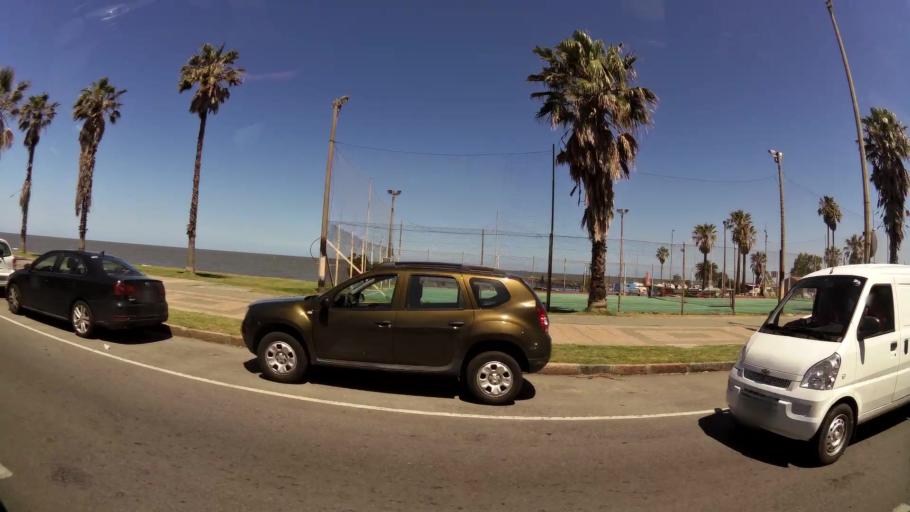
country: UY
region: Montevideo
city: Montevideo
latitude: -34.9227
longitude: -56.1520
